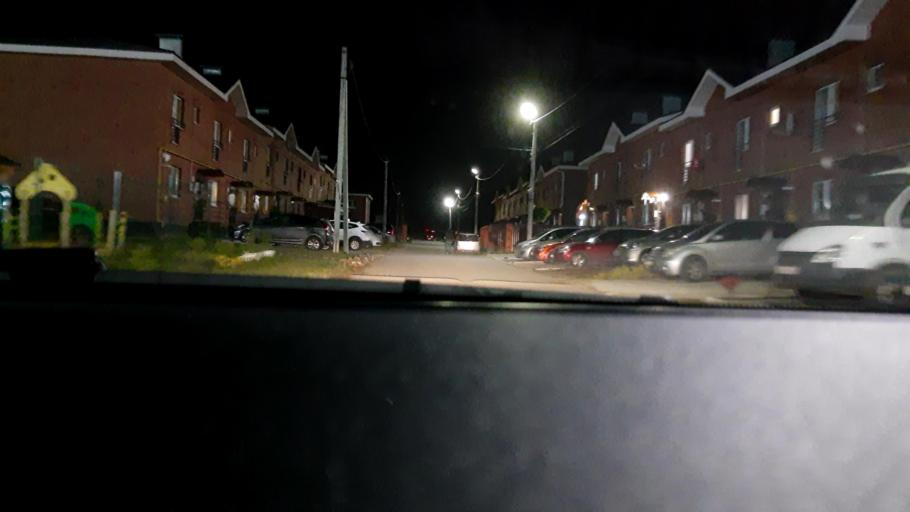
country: RU
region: Nizjnij Novgorod
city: Afonino
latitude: 56.2162
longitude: 44.0863
